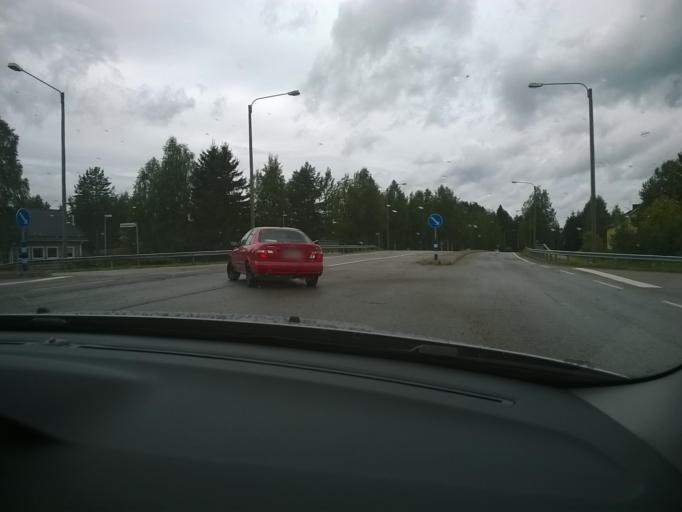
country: FI
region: Kainuu
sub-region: Kehys-Kainuu
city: Kuhmo
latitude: 64.1300
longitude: 29.4730
